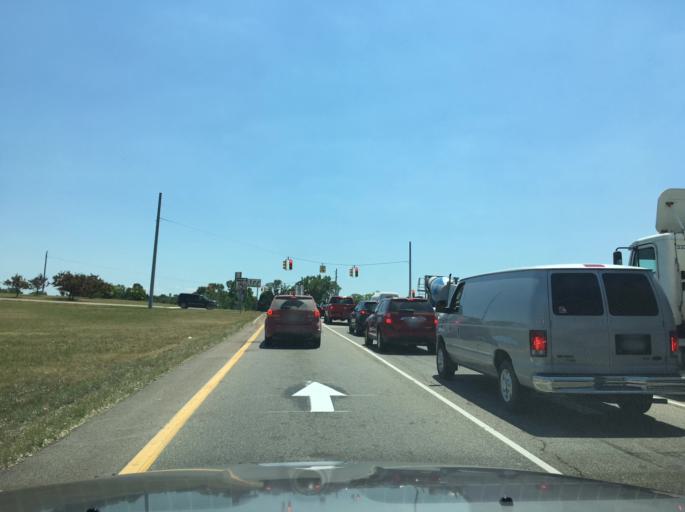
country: US
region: Michigan
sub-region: Macomb County
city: Utica
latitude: 42.6268
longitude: -83.0152
